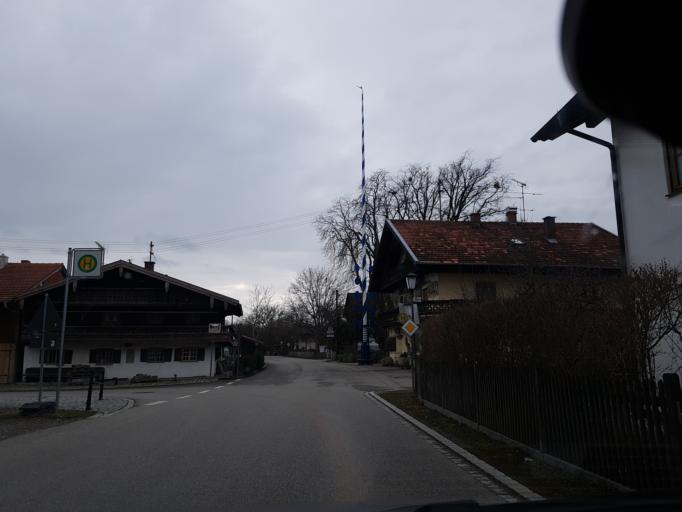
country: DE
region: Bavaria
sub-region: Upper Bavaria
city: Bruckmuhl
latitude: 47.9065
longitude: 11.9176
